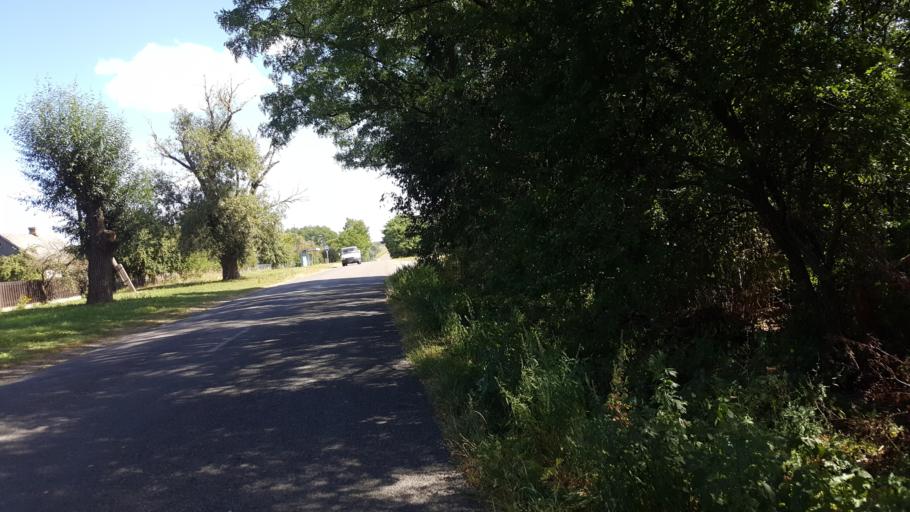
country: BY
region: Brest
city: Vysokaye
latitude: 52.2798
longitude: 23.3406
